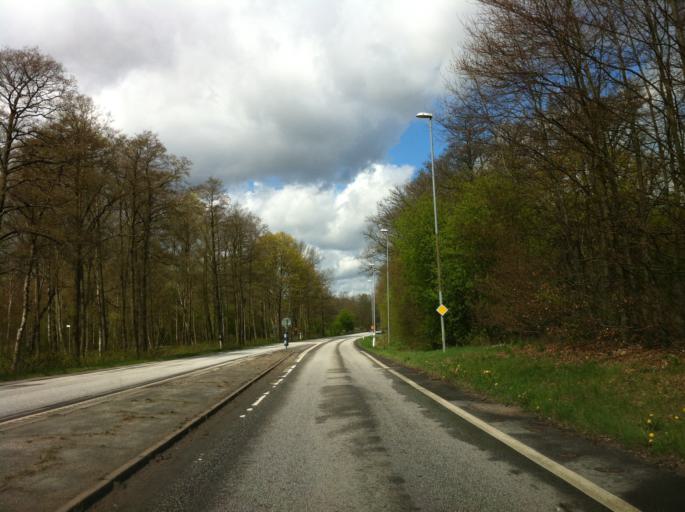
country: SE
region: Skane
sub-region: Hoors Kommun
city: Satofta
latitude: 55.9316
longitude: 13.5625
